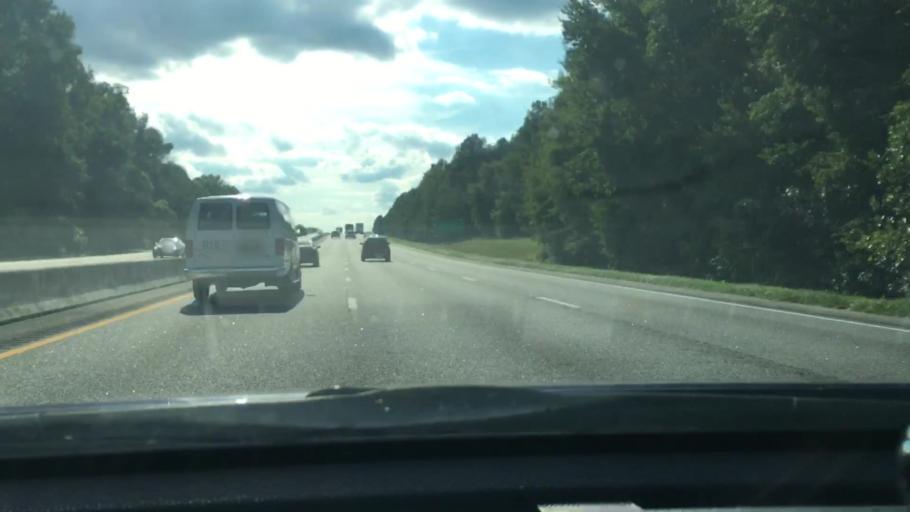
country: US
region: South Carolina
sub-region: Richland County
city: Forest Acres
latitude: 34.0702
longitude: -81.0144
